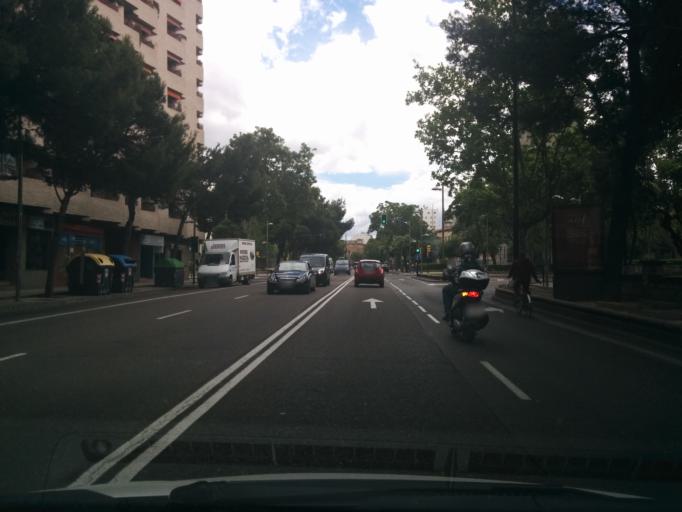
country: ES
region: Aragon
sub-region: Provincia de Zaragoza
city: Zaragoza
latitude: 41.6359
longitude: -0.8847
